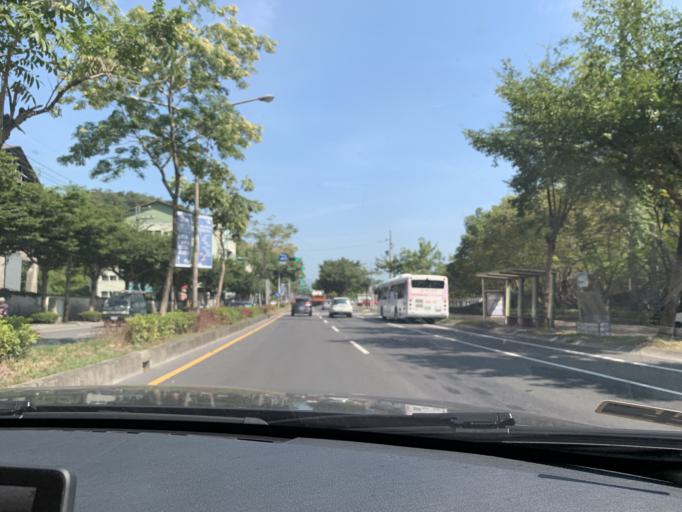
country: TW
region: Taiwan
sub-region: Yilan
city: Yilan
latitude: 24.6086
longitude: 121.8268
